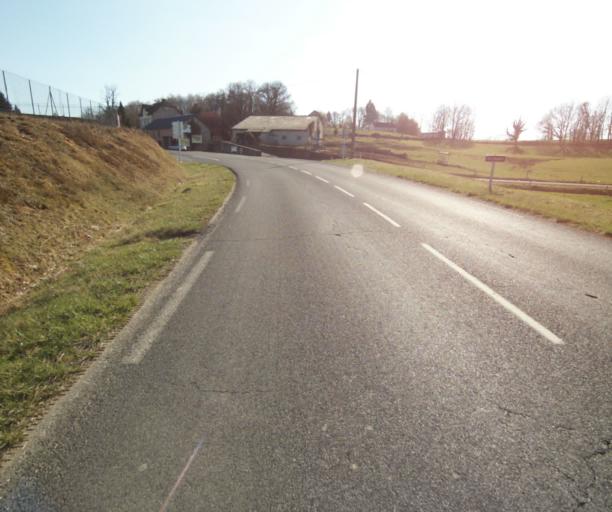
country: FR
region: Limousin
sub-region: Departement de la Correze
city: Saint-Clement
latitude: 45.3159
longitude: 1.6794
